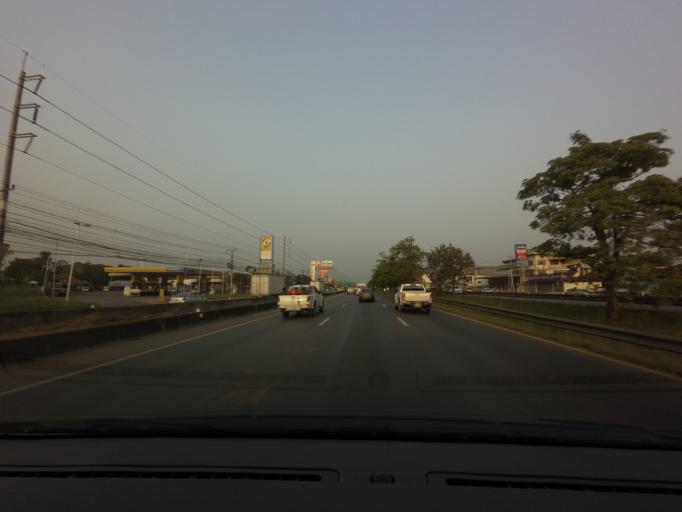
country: TH
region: Samut Sakhon
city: Samut Sakhon
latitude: 13.5774
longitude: 100.3021
